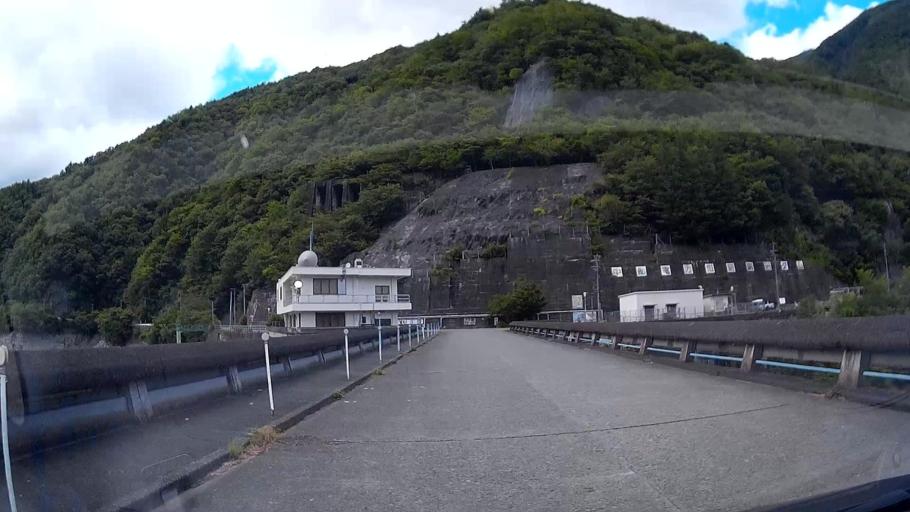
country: JP
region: Shizuoka
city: Shizuoka-shi
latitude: 35.3221
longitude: 138.1835
